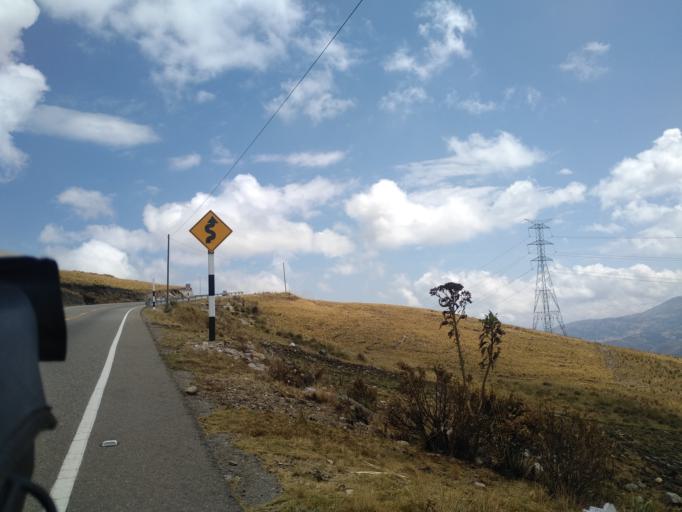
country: PE
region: La Libertad
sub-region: Provincia de Santiago de Chuco
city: Quiruvilca
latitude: -7.9229
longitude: -78.1548
